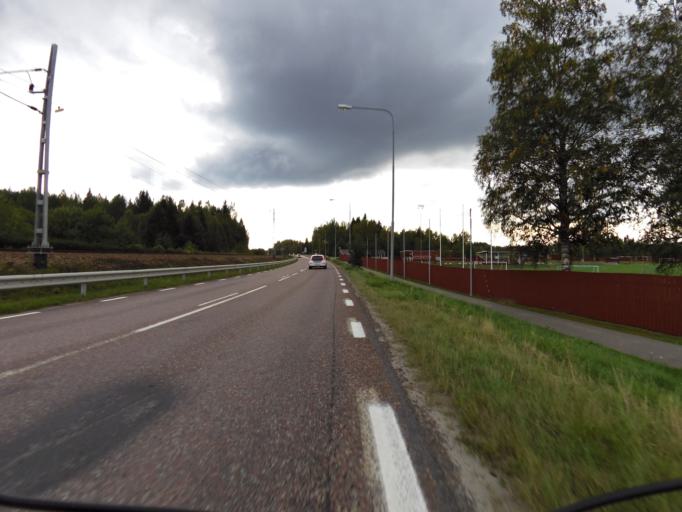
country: SE
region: Gaevleborg
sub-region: Ockelbo Kommun
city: Ockelbo
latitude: 60.8755
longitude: 16.7066
